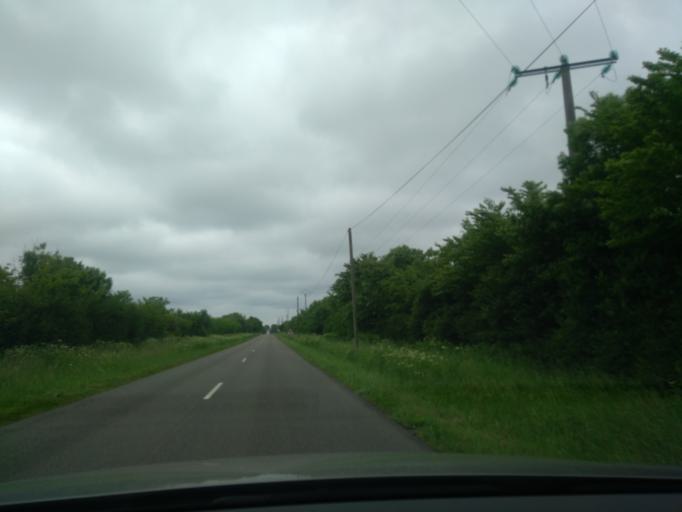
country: FR
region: Lower Normandy
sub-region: Departement de la Manche
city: Sainte-Mere-Eglise
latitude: 49.4489
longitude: -1.2785
